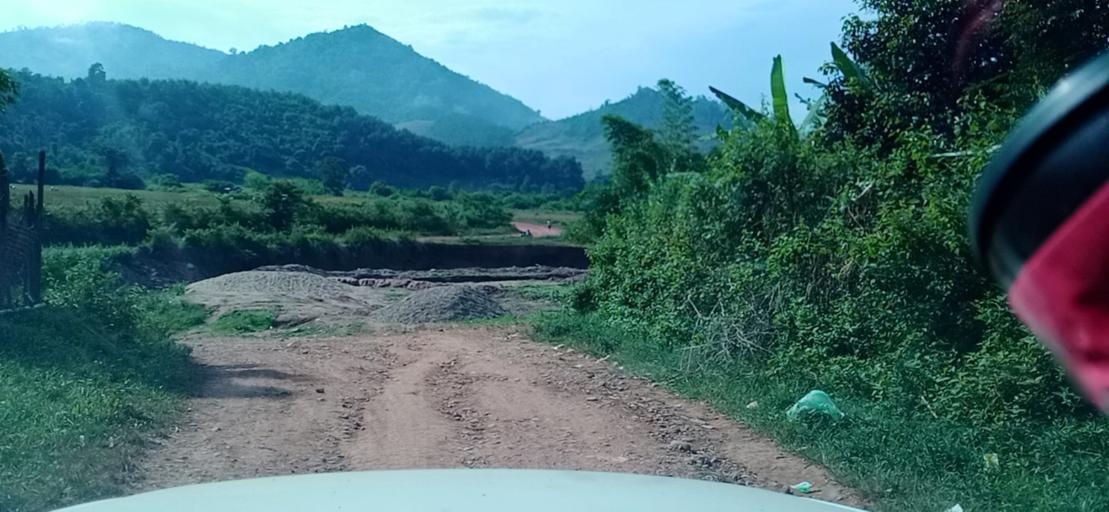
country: TH
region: Changwat Bueng Kan
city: Pak Khat
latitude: 18.6760
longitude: 103.1946
